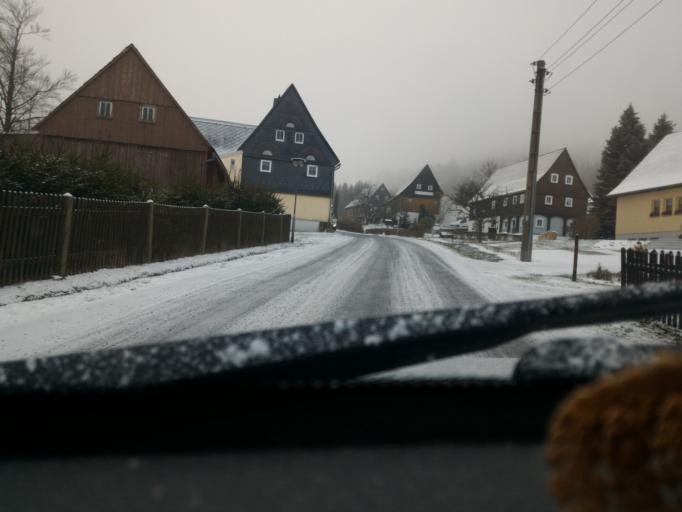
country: DE
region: Saxony
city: Grossschonau
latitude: 50.8565
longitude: 14.6544
